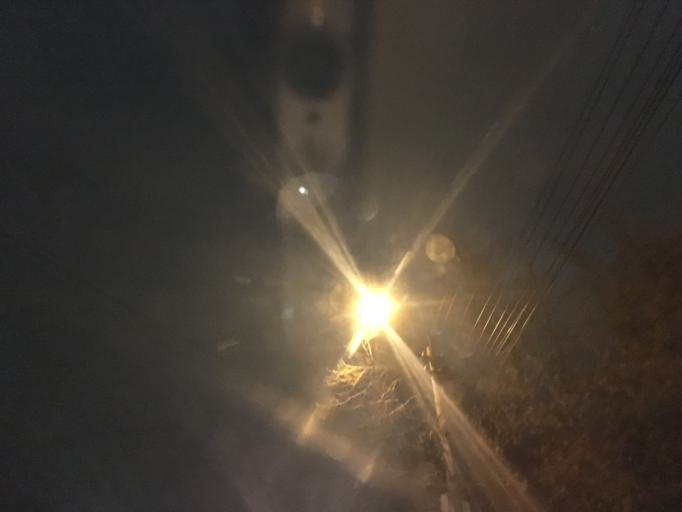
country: RU
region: Tula
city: Tula
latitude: 54.2140
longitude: 37.6198
